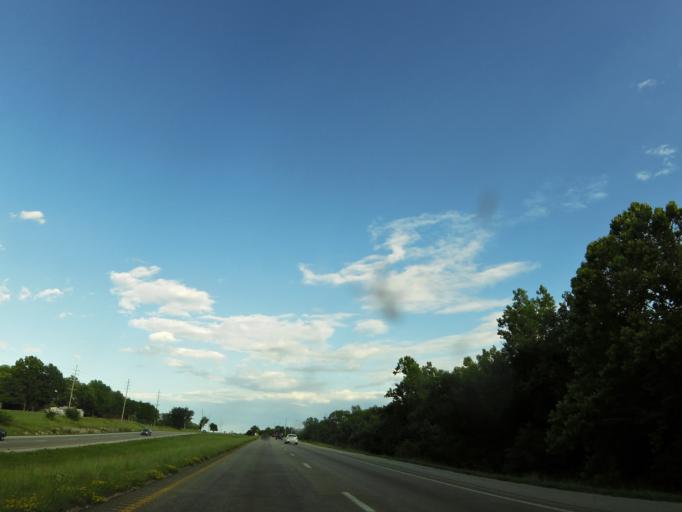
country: US
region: Missouri
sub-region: Lincoln County
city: Moscow Mills
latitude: 38.8789
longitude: -90.9129
